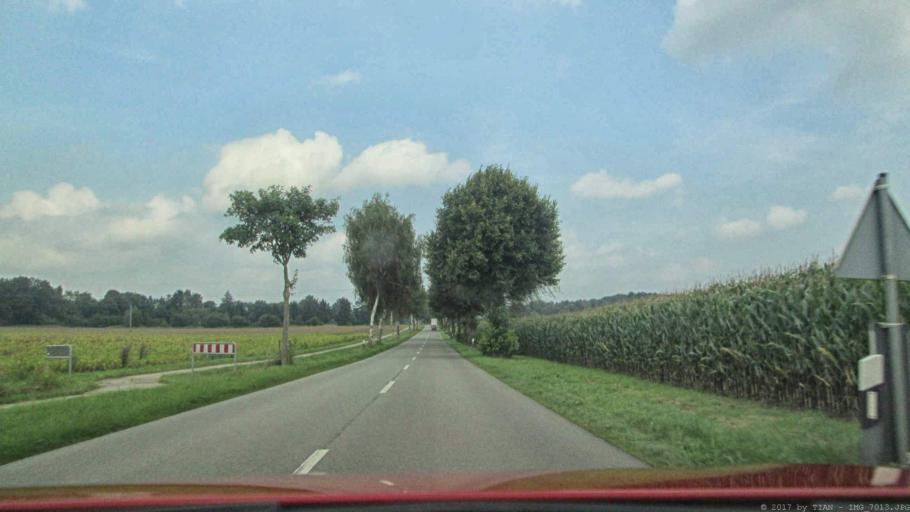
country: DE
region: Lower Saxony
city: Thomasburg
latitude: 53.1896
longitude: 10.6308
